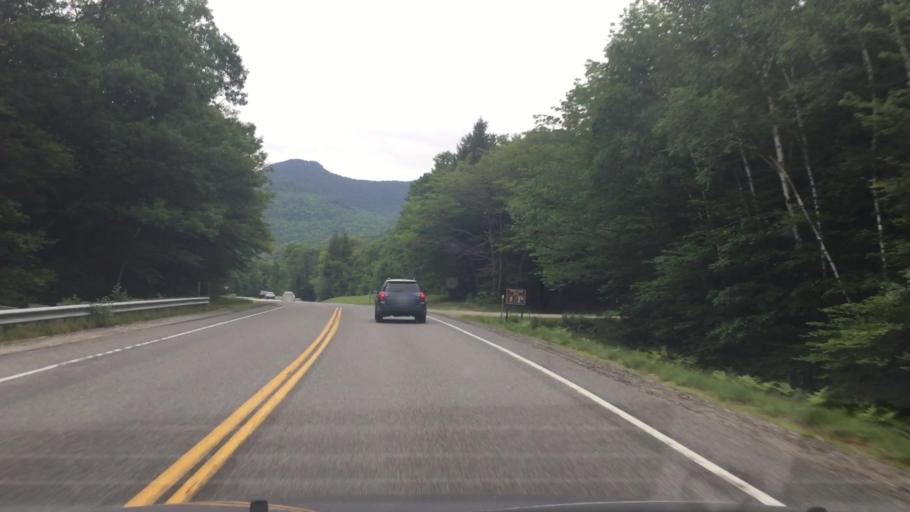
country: US
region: New Hampshire
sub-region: Carroll County
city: North Conway
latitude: 44.0871
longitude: -71.3521
